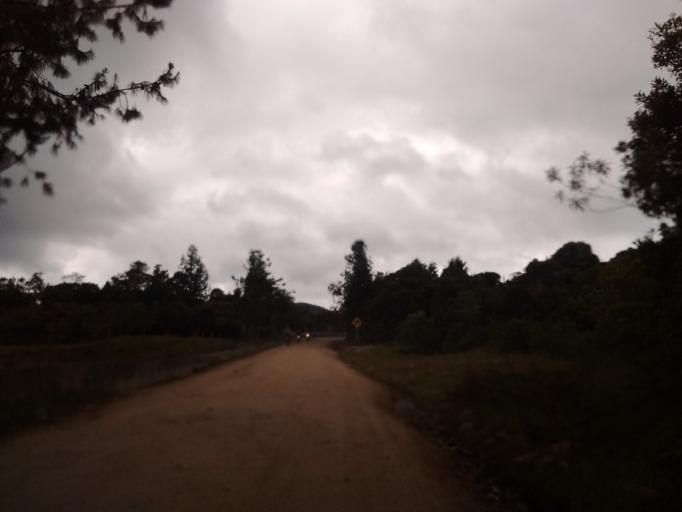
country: CO
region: Huila
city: Isnos
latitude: 2.0342
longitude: -76.2769
